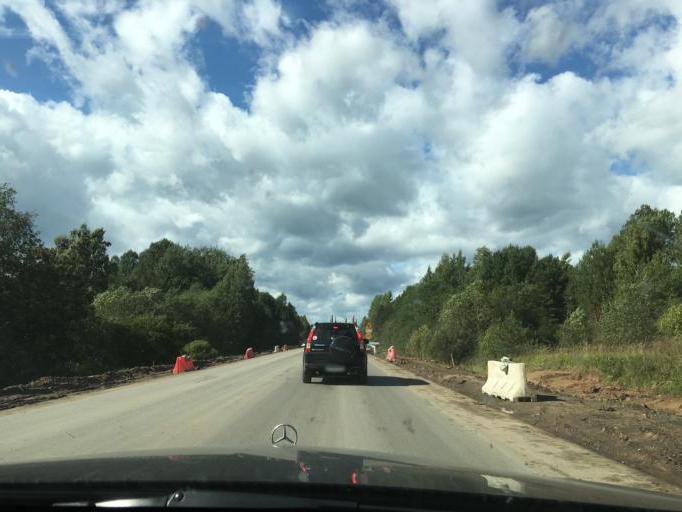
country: RU
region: Pskov
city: Novosokol'niki
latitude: 56.2811
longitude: 30.3002
